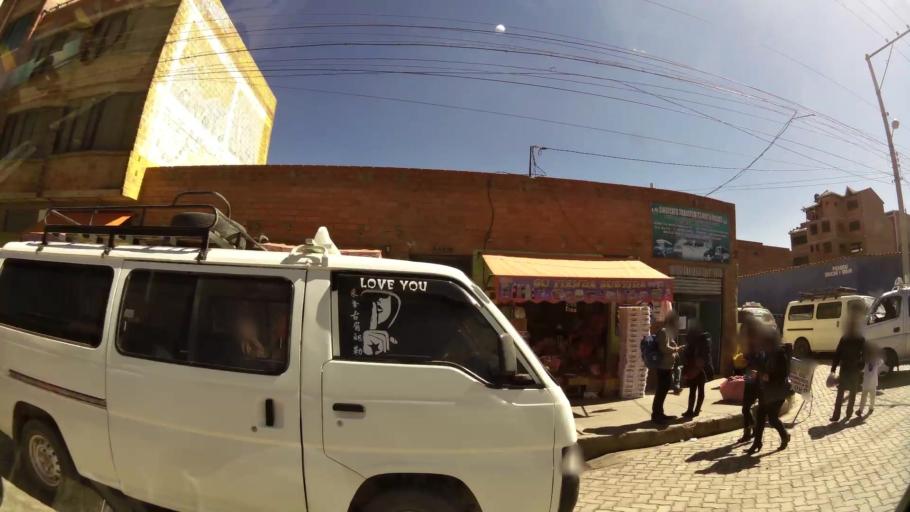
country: BO
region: La Paz
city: La Paz
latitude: -16.5345
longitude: -68.1919
